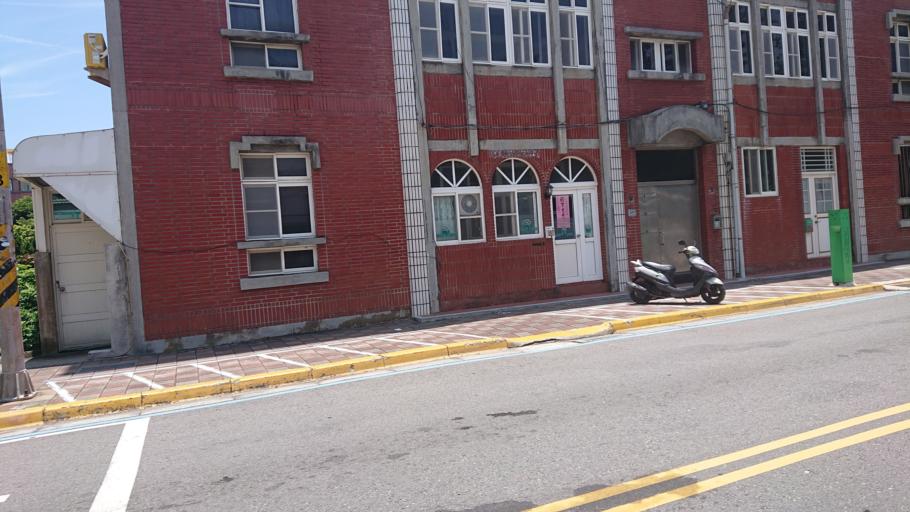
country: TW
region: Taiwan
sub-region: Penghu
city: Ma-kung
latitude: 23.5696
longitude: 119.5676
